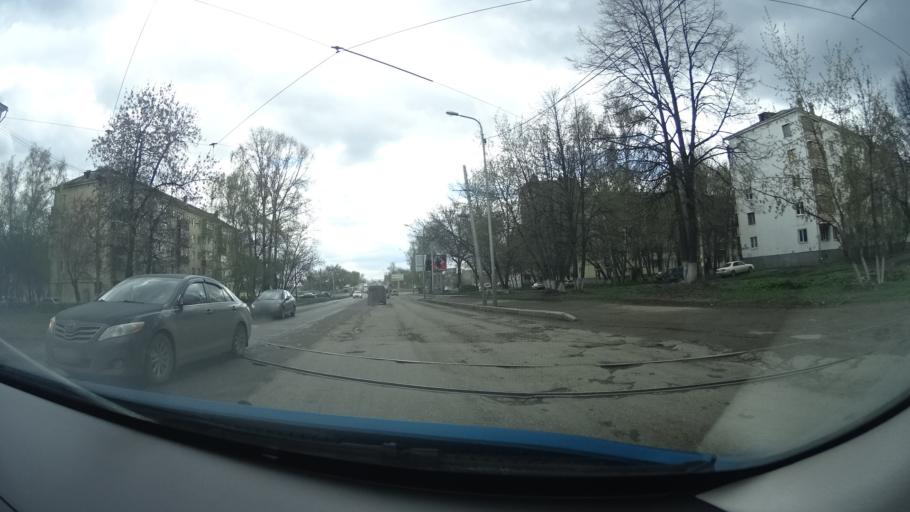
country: RU
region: Bashkortostan
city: Ufa
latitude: 54.8121
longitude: 56.0886
